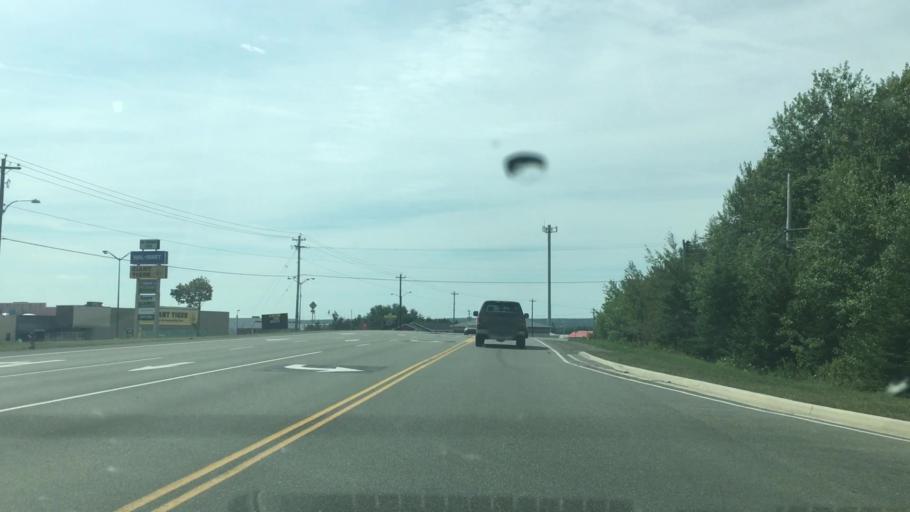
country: CA
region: Nova Scotia
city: Port Hawkesbury
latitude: 45.6180
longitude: -61.3354
